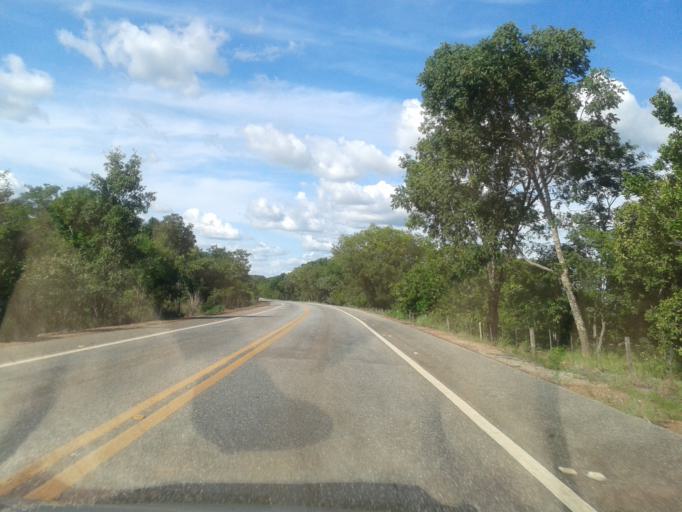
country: BR
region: Goias
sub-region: Mozarlandia
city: Mozarlandia
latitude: -14.8631
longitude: -50.5476
